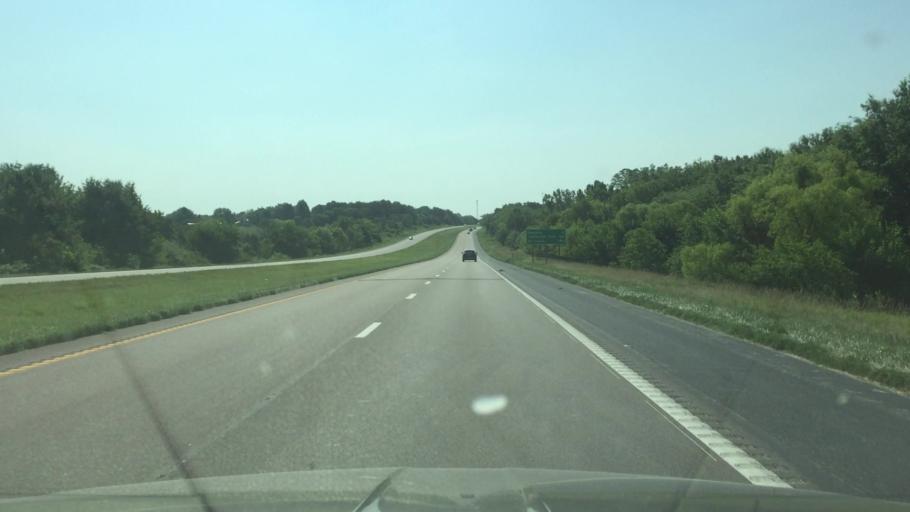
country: US
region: Missouri
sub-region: Pettis County
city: La Monte
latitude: 38.7434
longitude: -93.3300
